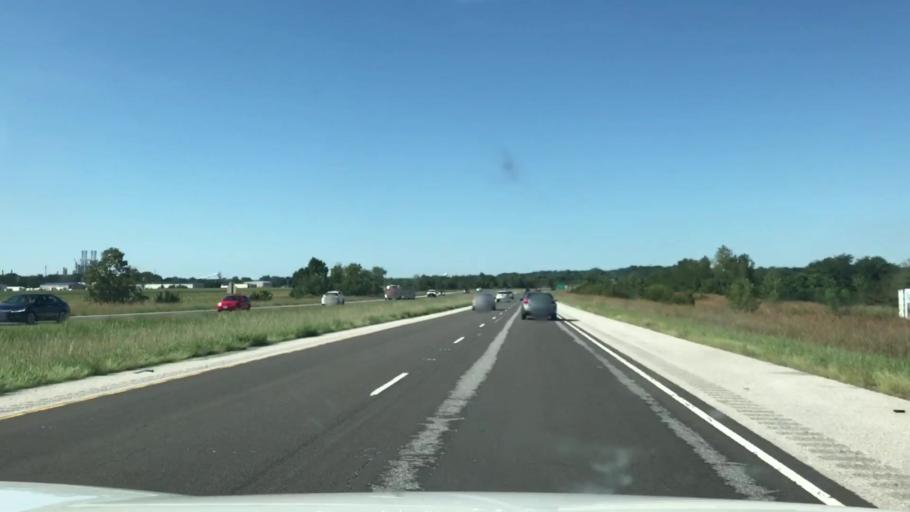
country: US
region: Illinois
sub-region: Madison County
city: South Roxana
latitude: 38.8216
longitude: -90.0426
